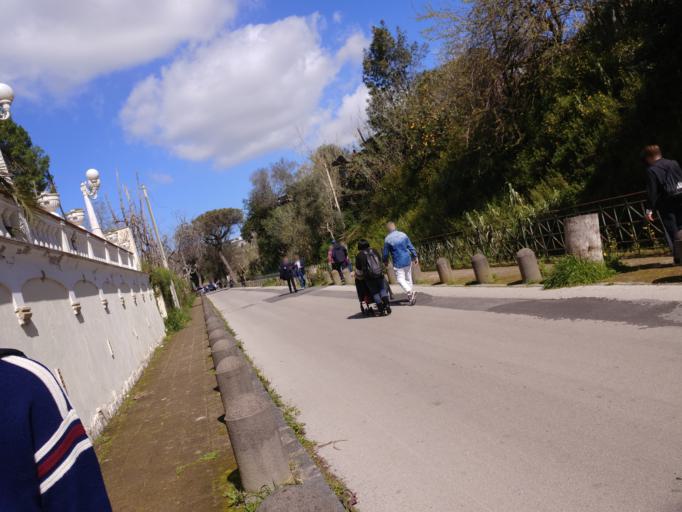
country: IT
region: Campania
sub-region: Provincia di Napoli
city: Monterusciello
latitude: 40.8331
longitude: 14.0806
